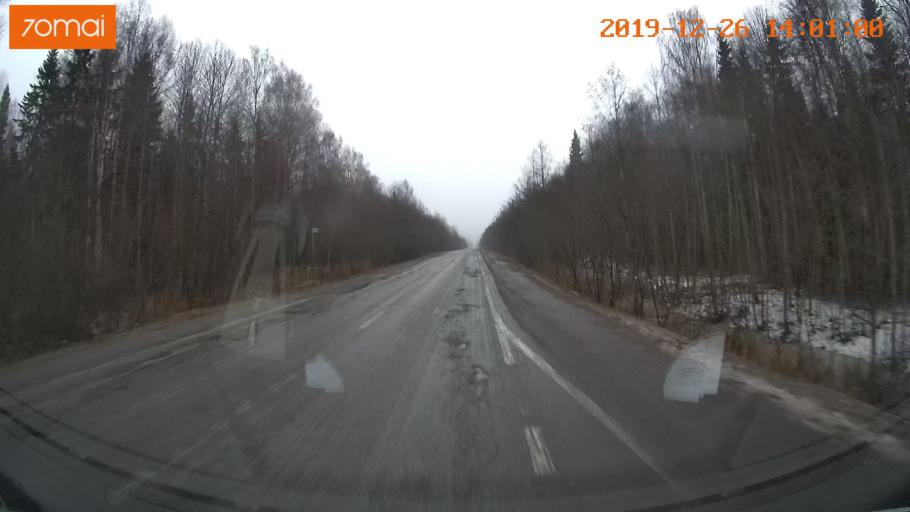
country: RU
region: Jaroslavl
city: Poshekhon'ye
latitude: 58.5538
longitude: 38.7550
